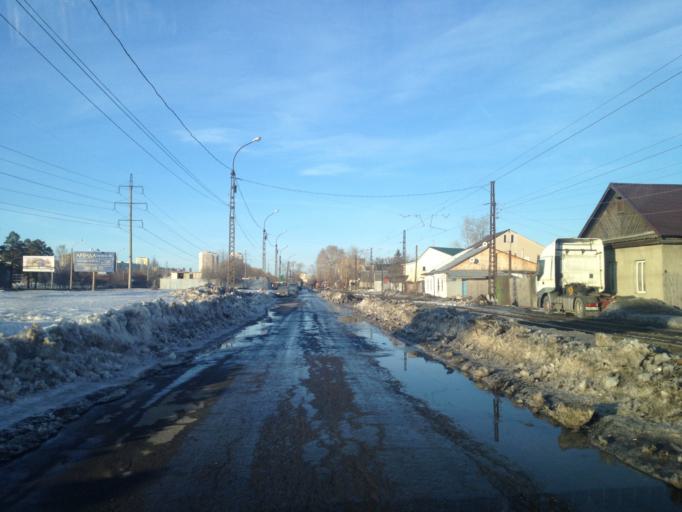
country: RU
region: Sverdlovsk
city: Sovkhoznyy
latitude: 56.7616
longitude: 60.5908
